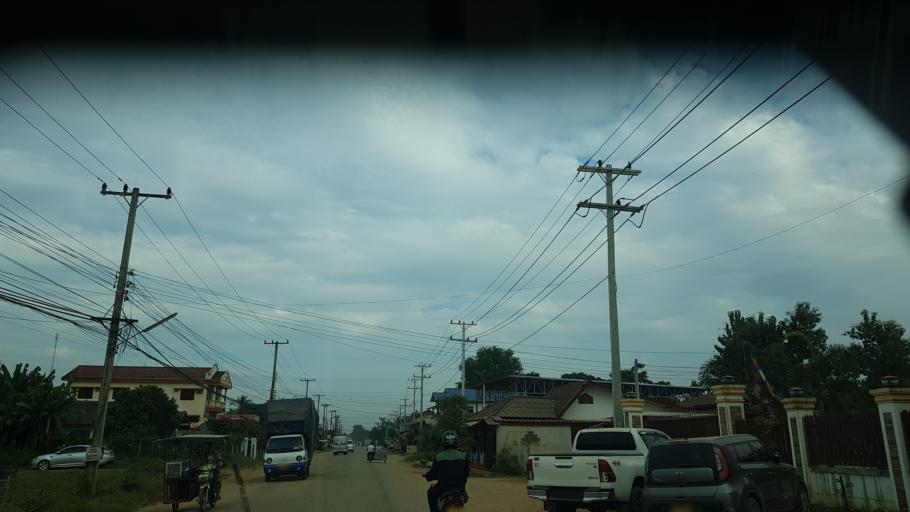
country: TH
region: Nong Khai
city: Nong Khai
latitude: 17.8873
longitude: 102.7290
